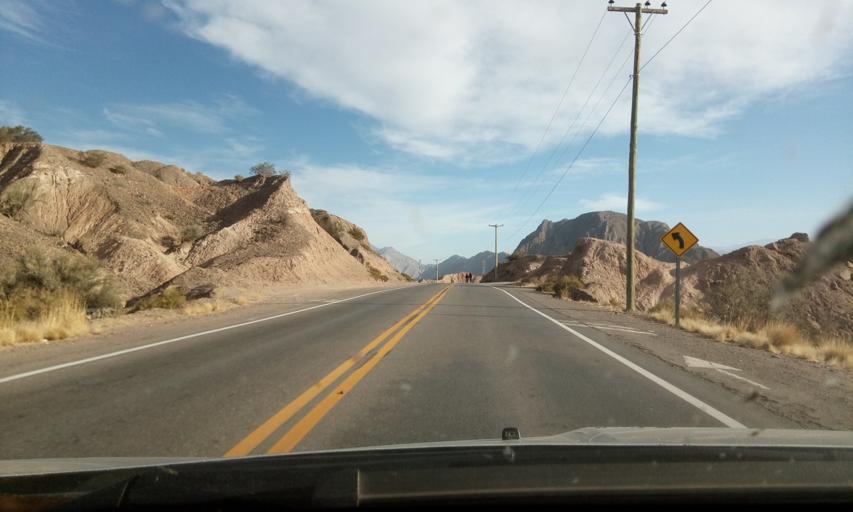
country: AR
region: San Juan
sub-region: Departamento de Rivadavia
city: Rivadavia
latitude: -31.4657
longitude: -68.6406
